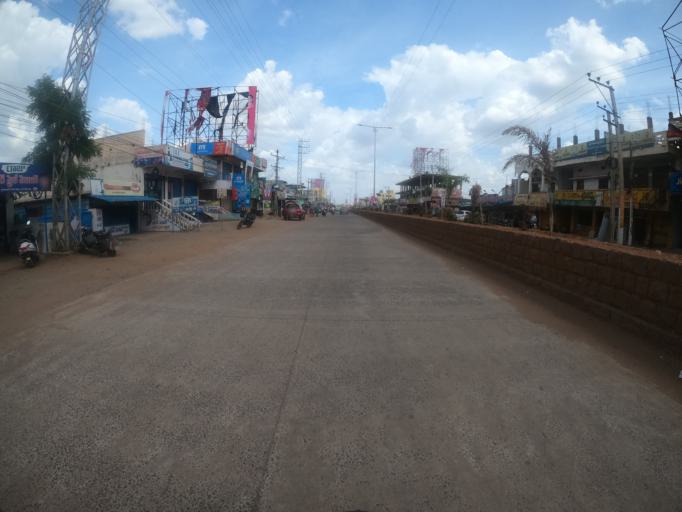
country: IN
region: Telangana
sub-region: Rangareddi
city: Sriramnagar
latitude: 17.3127
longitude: 78.1399
